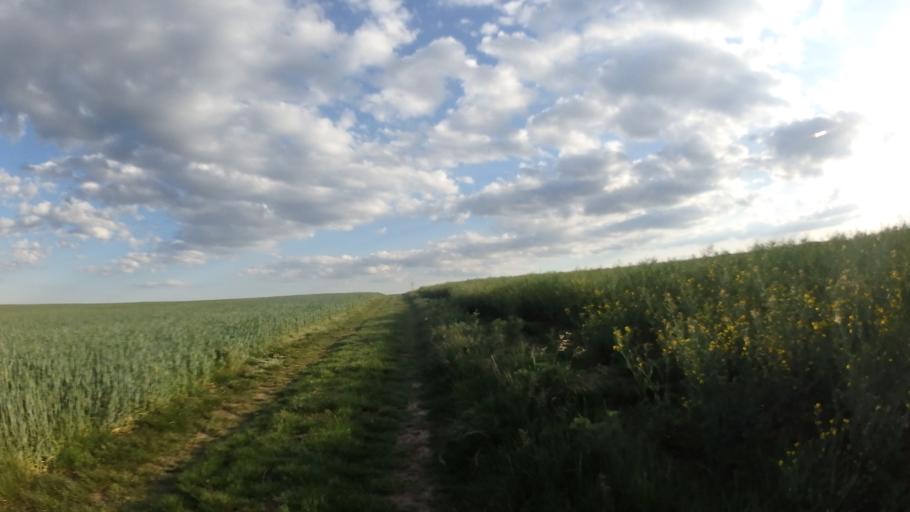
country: CZ
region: South Moravian
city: Moravany
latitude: 49.1393
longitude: 16.5917
